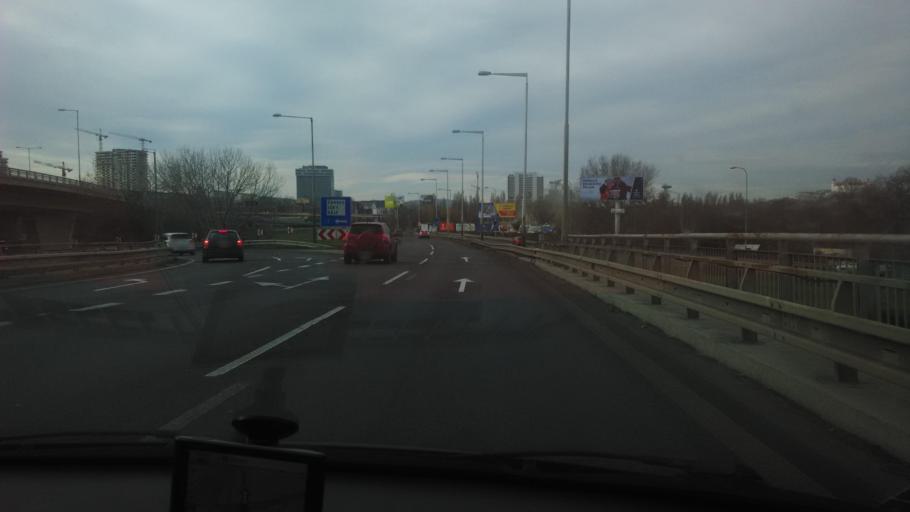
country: SK
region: Bratislavsky
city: Bratislava
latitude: 48.1317
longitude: 17.1300
